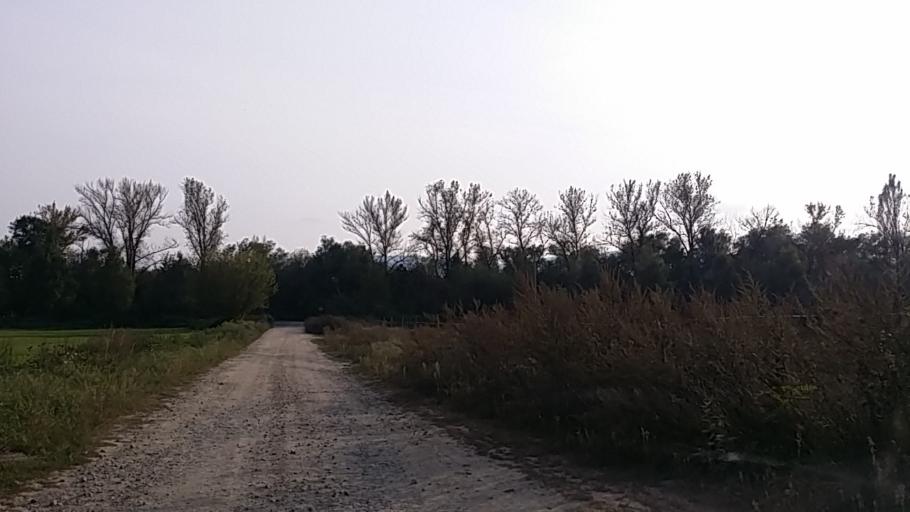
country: HU
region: Pest
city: Veroce
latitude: 47.8180
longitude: 19.0662
